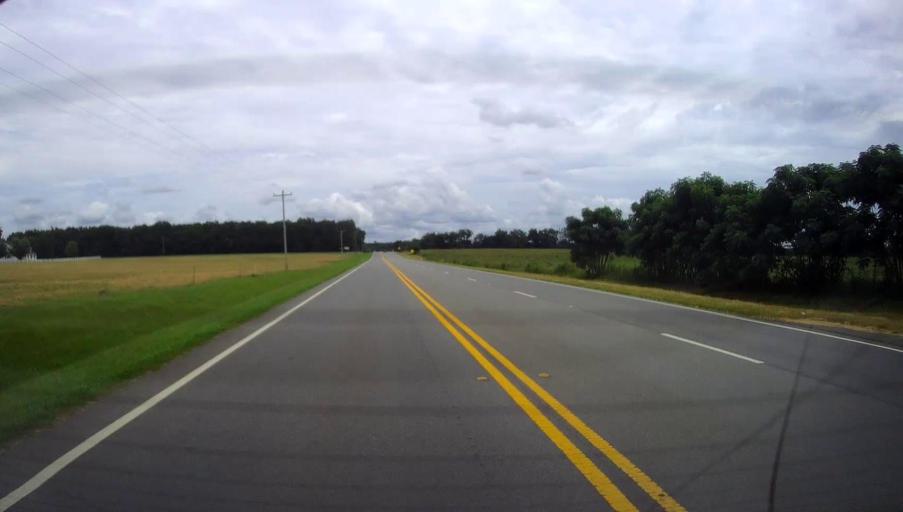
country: US
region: Georgia
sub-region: Macon County
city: Montezuma
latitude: 32.2922
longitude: -83.9331
